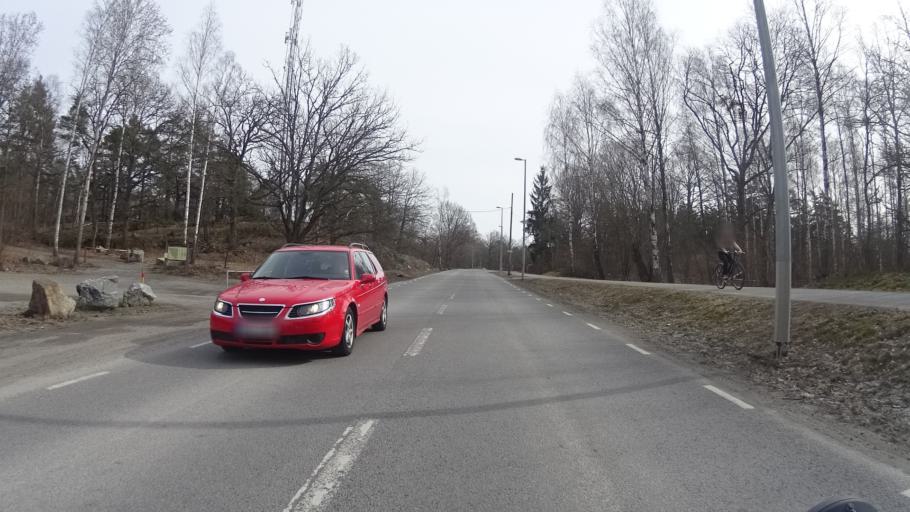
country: SE
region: Stockholm
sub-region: Nacka Kommun
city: Nacka
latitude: 59.2928
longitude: 18.1471
